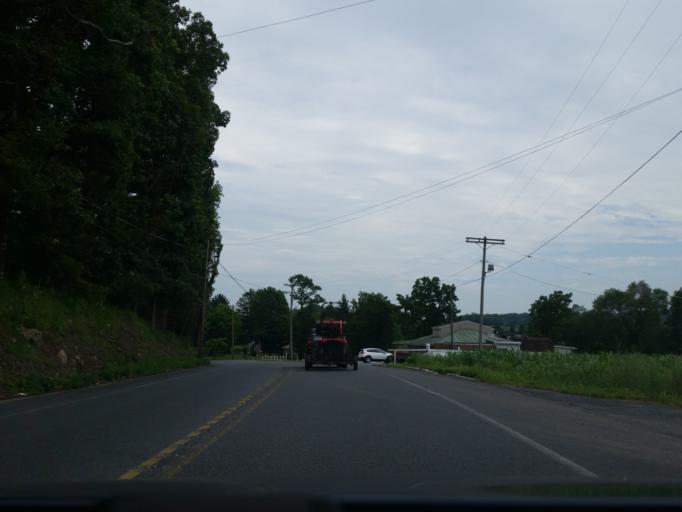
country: US
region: Pennsylvania
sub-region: Lebanon County
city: Jonestown
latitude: 40.3981
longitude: -76.4903
